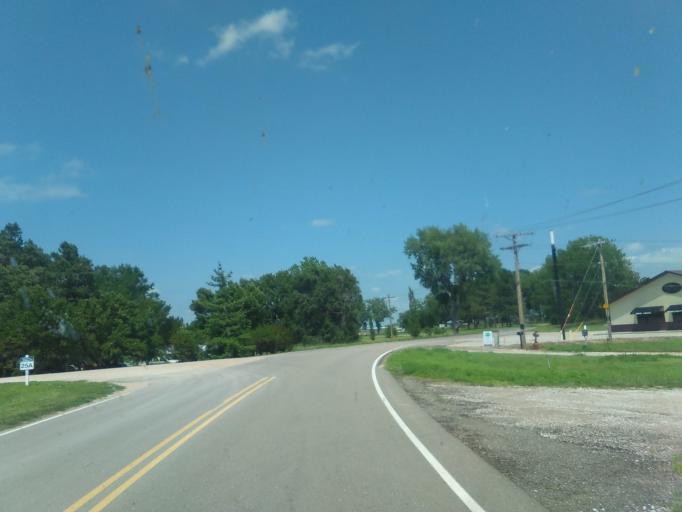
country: US
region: Nebraska
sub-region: Gosper County
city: Elwood
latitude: 40.6843
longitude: -99.8282
